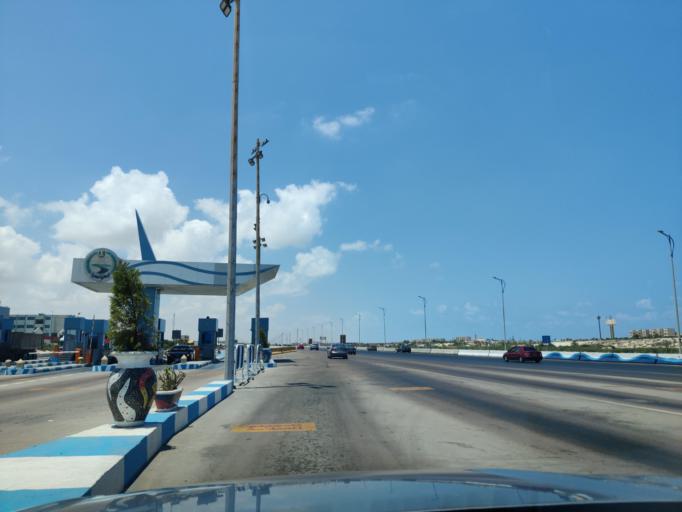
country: EG
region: Muhafazat Matruh
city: Al `Alamayn
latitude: 30.8984
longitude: 29.4099
